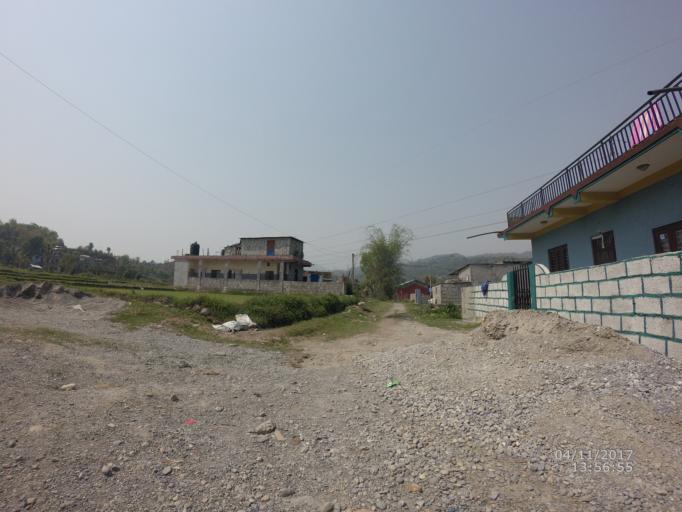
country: NP
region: Western Region
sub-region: Gandaki Zone
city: Pokhara
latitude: 28.1865
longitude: 84.0425
